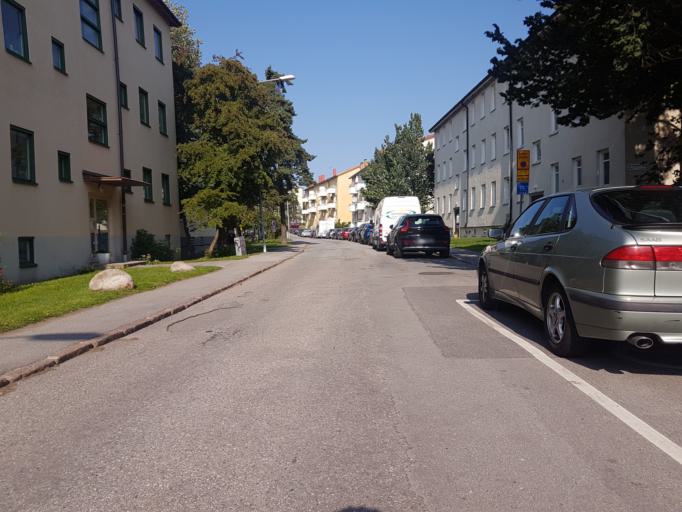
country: SE
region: Stockholm
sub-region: Stockholms Kommun
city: OEstermalm
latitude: 59.2960
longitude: 18.1047
